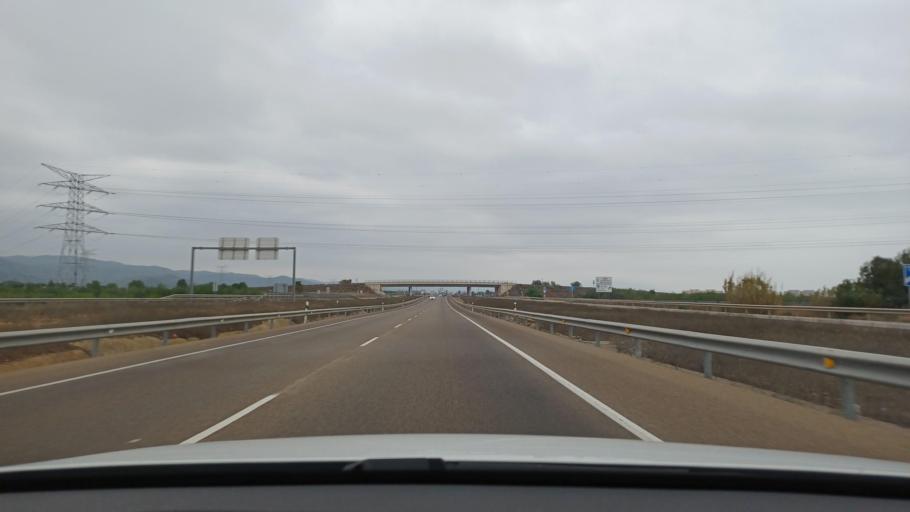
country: ES
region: Valencia
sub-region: Provincia de Castello
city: Orpesa/Oropesa del Mar
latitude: 40.1235
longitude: 0.1440
